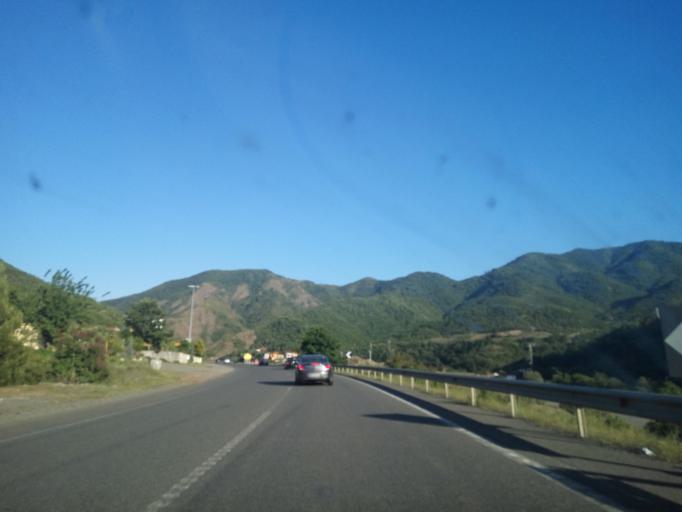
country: AL
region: Lezhe
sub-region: Rrethi i Mirdites
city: Rubik
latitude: 41.7849
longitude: 19.8210
